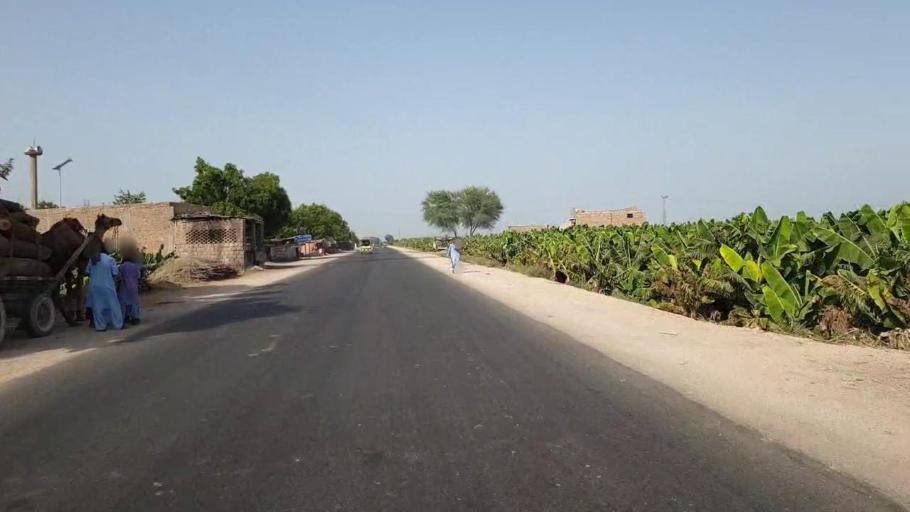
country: PK
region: Sindh
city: Sakrand
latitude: 26.2477
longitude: 68.2974
